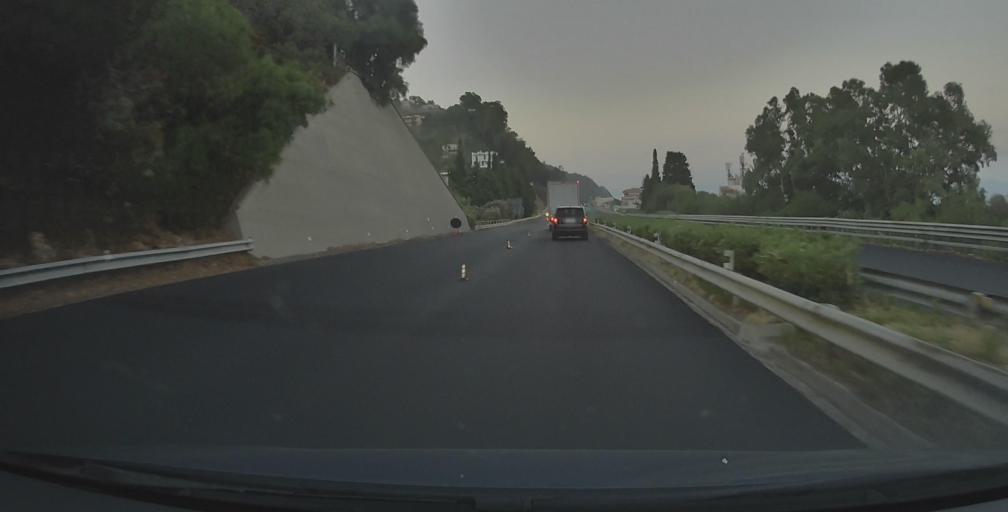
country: IT
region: Sicily
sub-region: Messina
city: Guidomandri Marina
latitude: 38.0385
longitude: 15.4531
